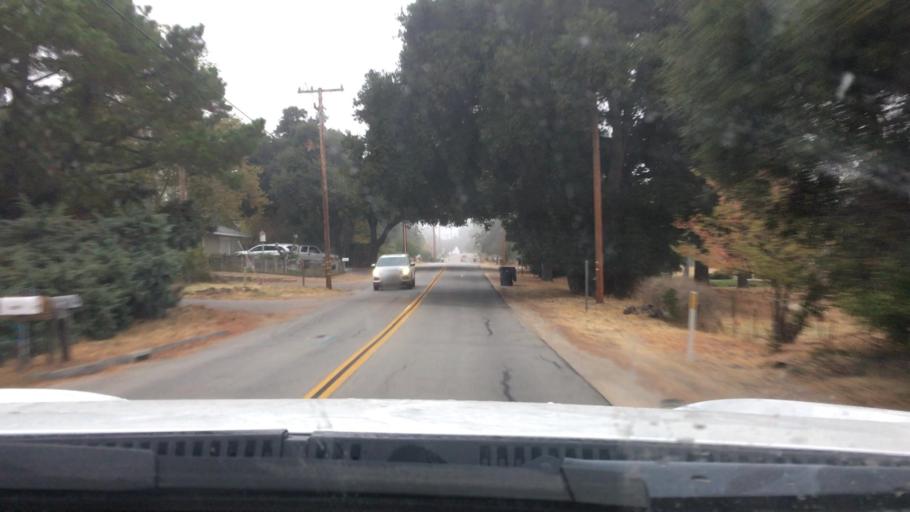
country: US
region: California
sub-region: San Luis Obispo County
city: Atascadero
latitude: 35.4860
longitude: -120.6852
